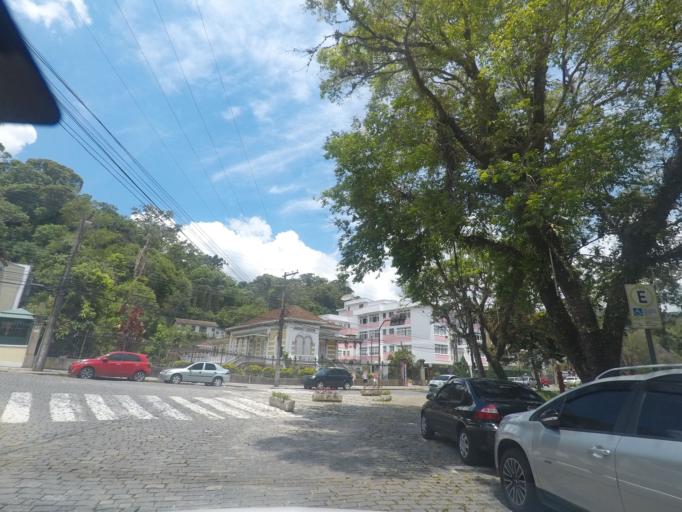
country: BR
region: Rio de Janeiro
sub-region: Petropolis
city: Petropolis
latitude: -22.5064
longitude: -43.1776
